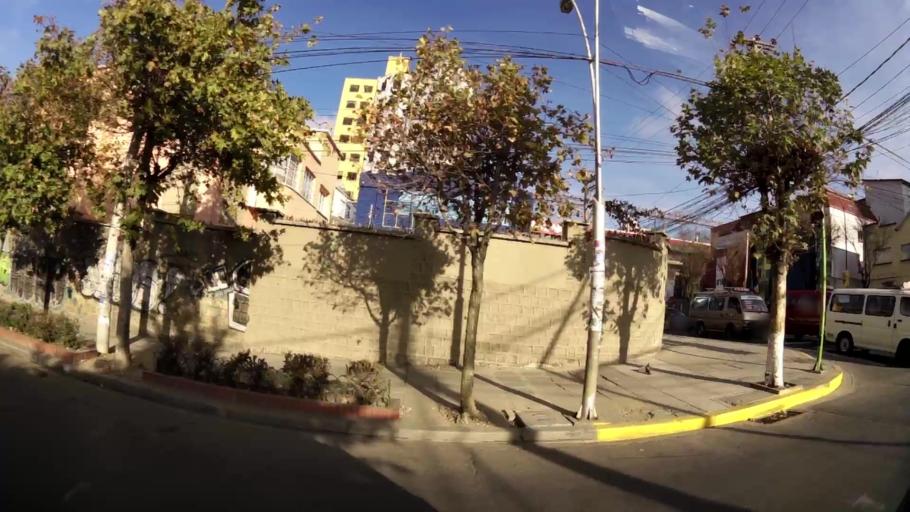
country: BO
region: La Paz
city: La Paz
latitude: -16.4996
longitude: -68.1212
